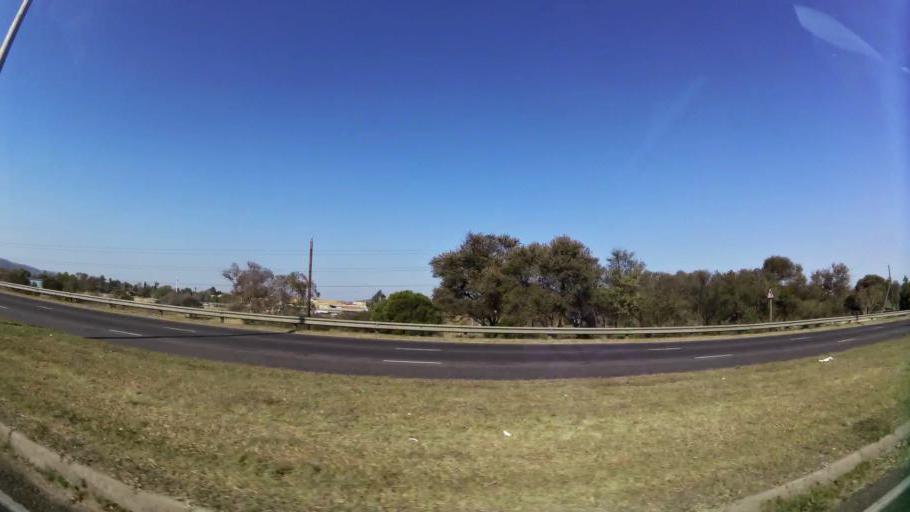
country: ZA
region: Gauteng
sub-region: City of Tshwane Metropolitan Municipality
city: Pretoria
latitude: -25.7140
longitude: 28.1707
